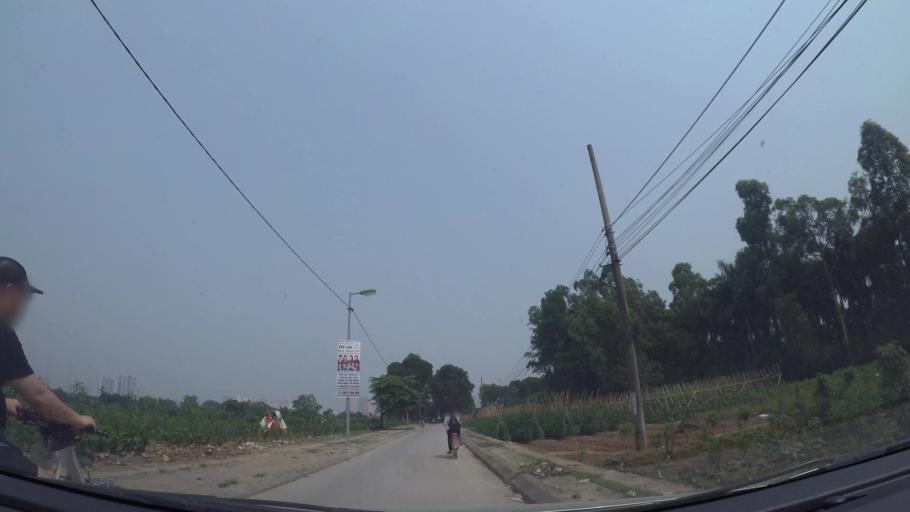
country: VN
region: Ha Noi
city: Ha Dong
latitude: 20.9943
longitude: 105.7648
